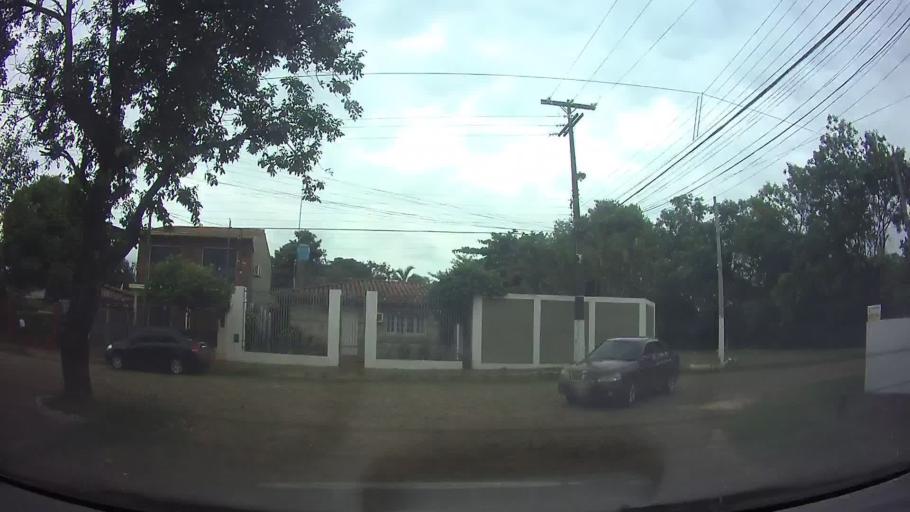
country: PY
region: Central
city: San Lorenzo
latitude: -25.2667
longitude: -57.4794
